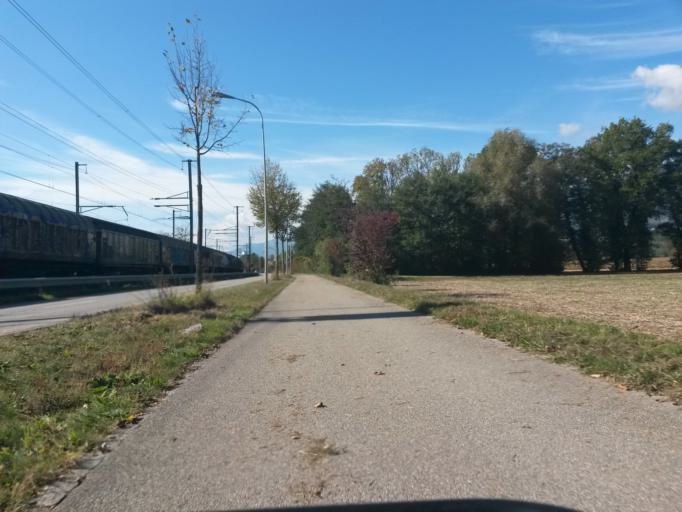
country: CH
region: Solothurn
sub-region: Bezirk Wasseramt
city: Luterbach
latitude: 47.2197
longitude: 7.5952
